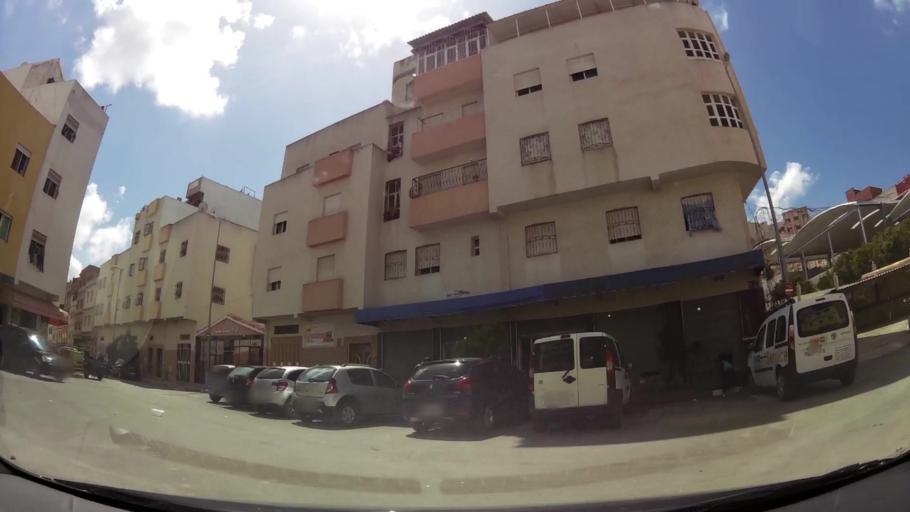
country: MA
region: Tanger-Tetouan
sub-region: Tanger-Assilah
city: Tangier
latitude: 35.7545
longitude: -5.8263
